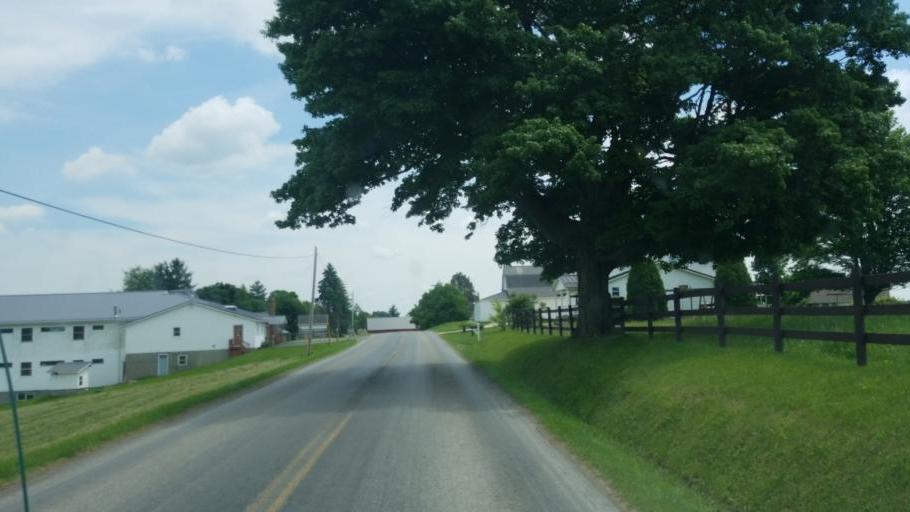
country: US
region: Ohio
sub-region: Tuscarawas County
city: Sugarcreek
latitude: 40.4478
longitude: -81.7685
